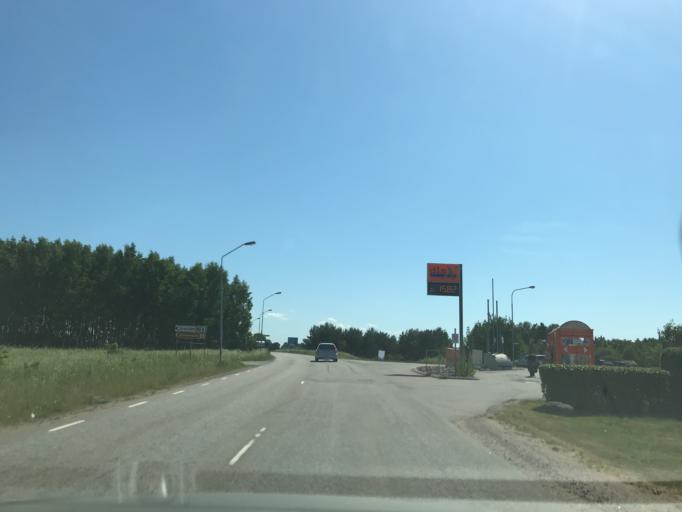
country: SE
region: Vaestra Goetaland
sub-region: Gotene Kommun
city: Kallby
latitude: 58.5063
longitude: 13.3106
